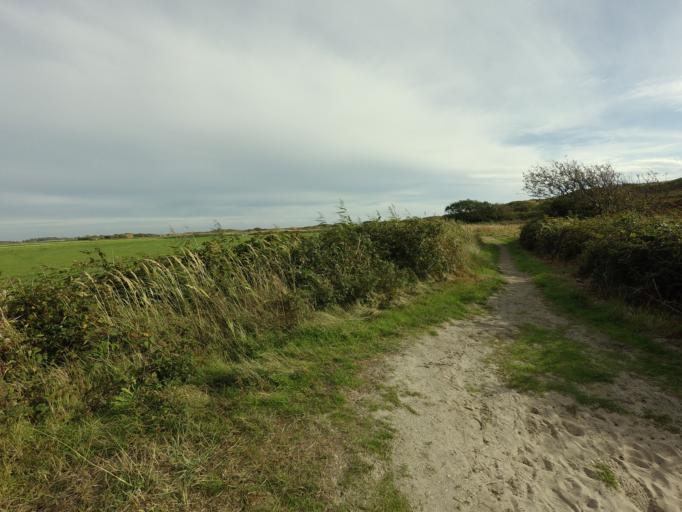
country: NL
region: North Holland
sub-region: Gemeente Den Helder
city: Den Helder
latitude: 53.0169
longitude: 4.7401
